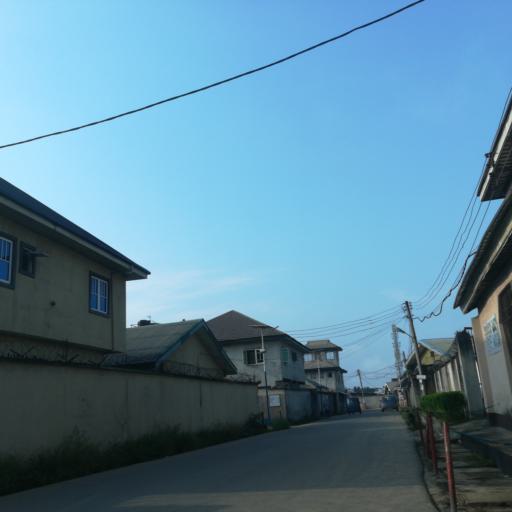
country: NG
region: Rivers
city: Port Harcourt
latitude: 4.8559
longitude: 6.9629
